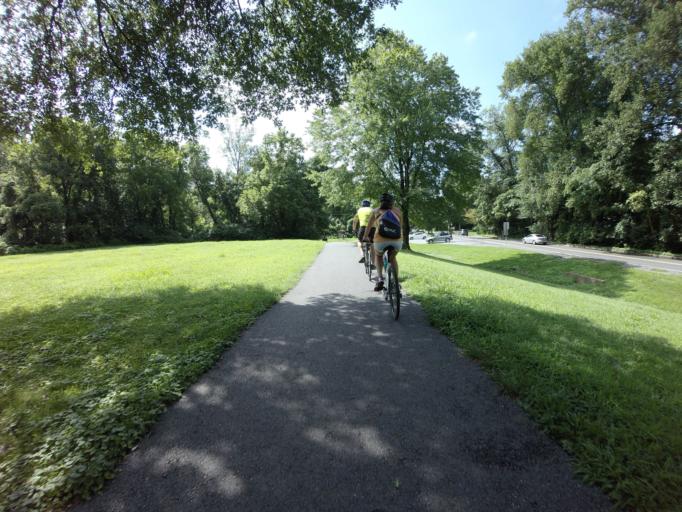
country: US
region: Maryland
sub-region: Montgomery County
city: Forest Glen
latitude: 39.0091
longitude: -77.0630
